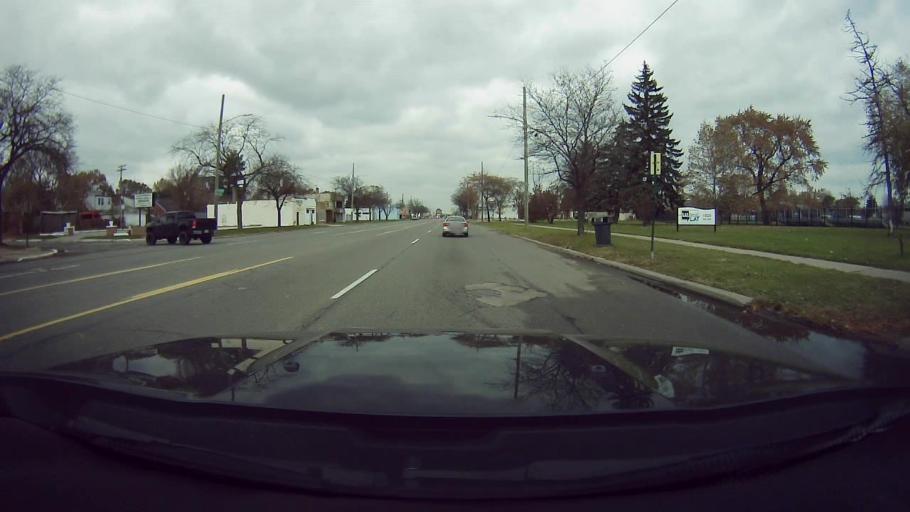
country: US
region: Michigan
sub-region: Macomb County
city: Warren
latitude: 42.4359
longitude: -83.0242
